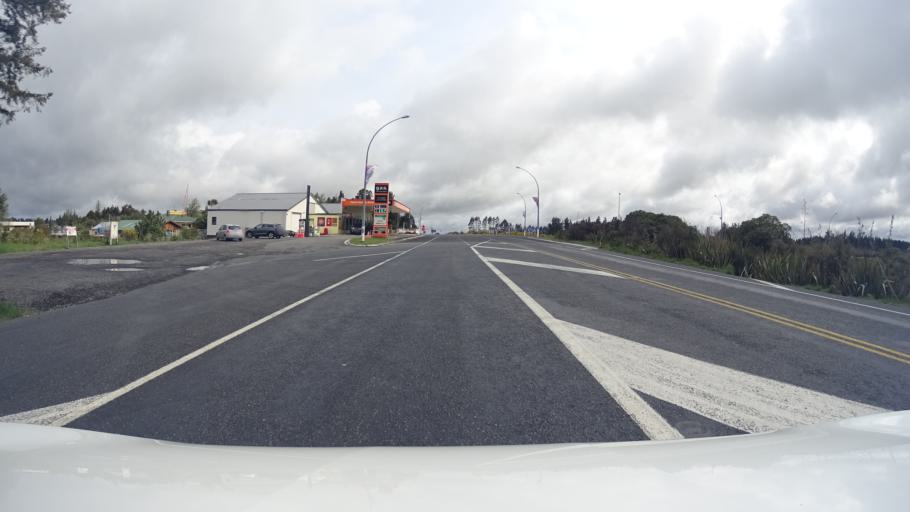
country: NZ
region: Manawatu-Wanganui
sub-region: Ruapehu District
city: Waiouru
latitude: -39.1777
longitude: 175.4024
